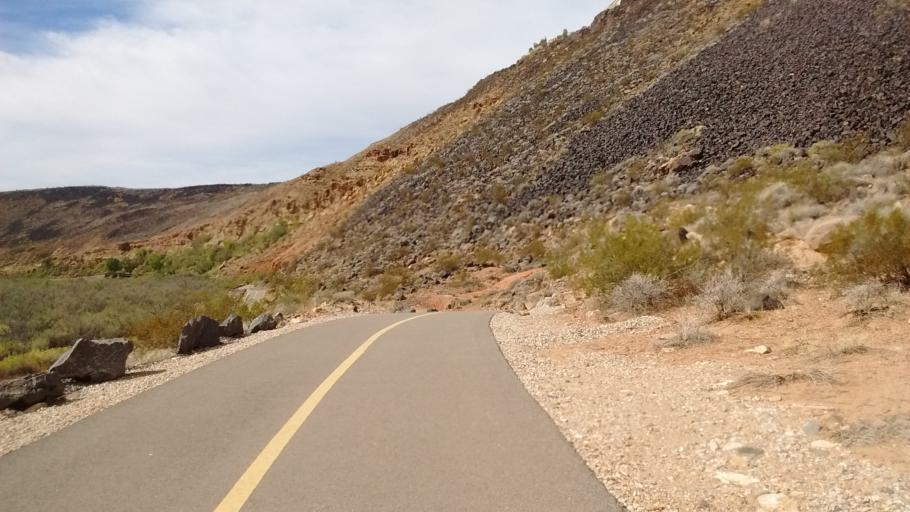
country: US
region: Utah
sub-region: Washington County
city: Washington
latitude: 37.1236
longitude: -113.4870
